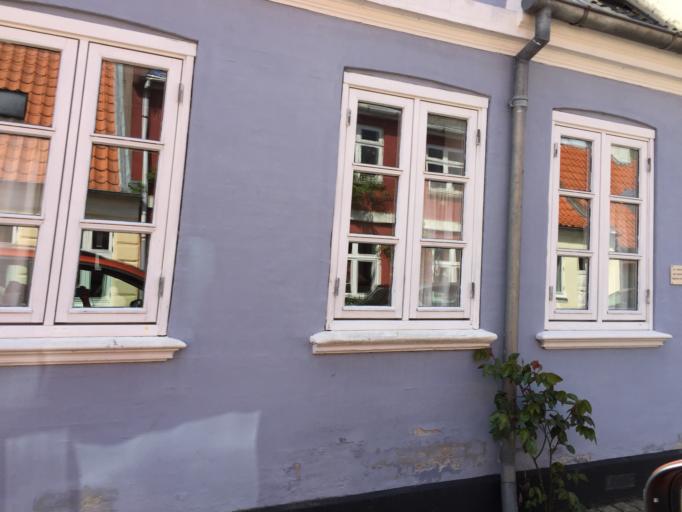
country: DK
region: South Denmark
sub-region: Middelfart Kommune
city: Middelfart
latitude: 55.5050
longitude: 9.7278
